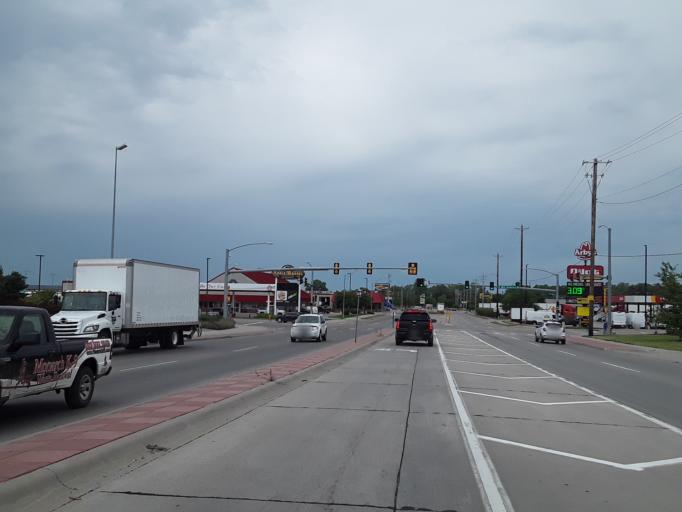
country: US
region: Iowa
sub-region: Pottawattamie County
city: Council Bluffs
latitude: 41.2342
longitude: -95.8792
